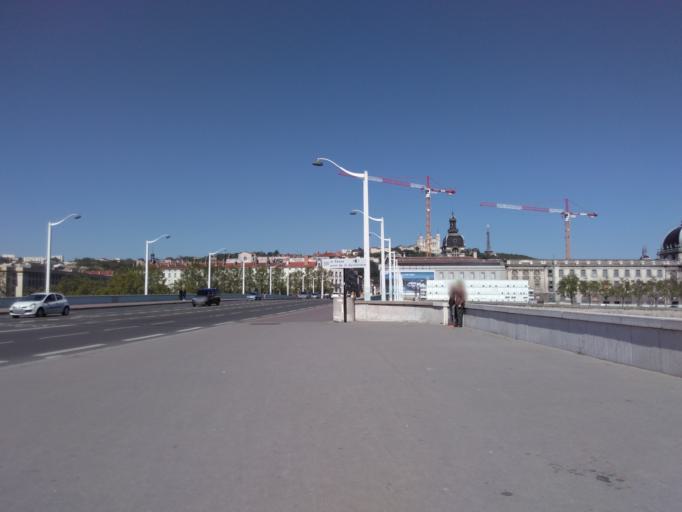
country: FR
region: Rhone-Alpes
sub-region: Departement du Rhone
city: Lyon
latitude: 45.7565
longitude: 4.8400
